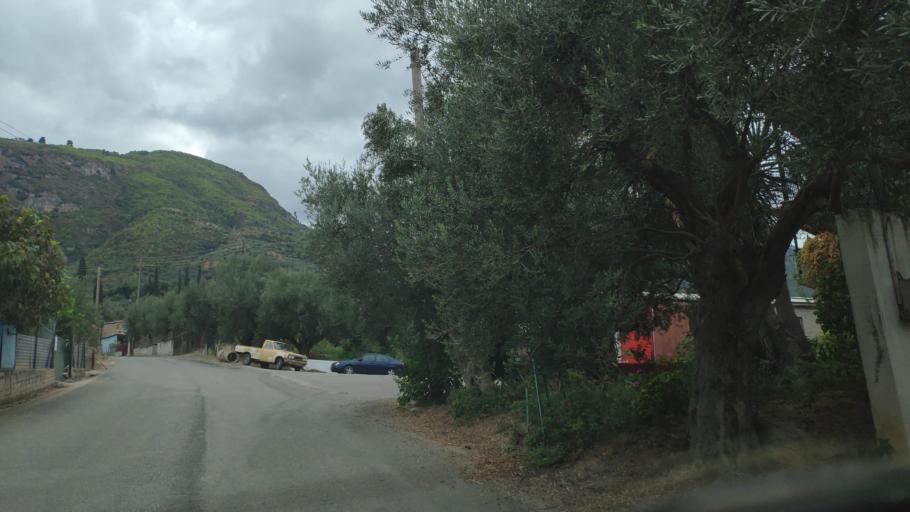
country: GR
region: West Greece
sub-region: Nomos Achaias
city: Temeni
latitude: 38.1801
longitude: 22.1443
